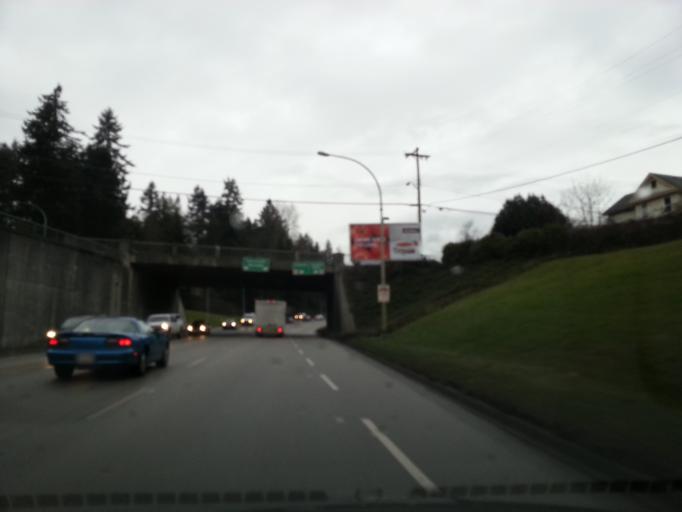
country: CA
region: British Columbia
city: New Westminster
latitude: 49.2109
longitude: -122.8999
